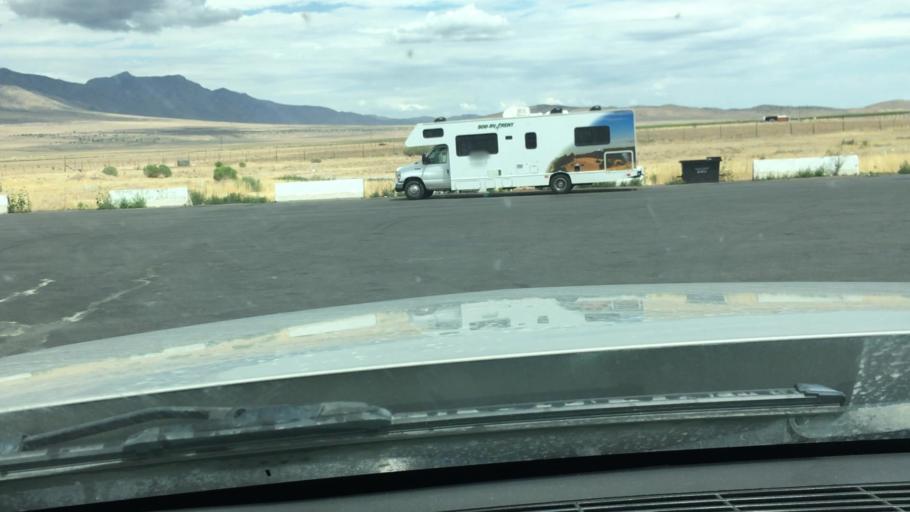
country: US
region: Utah
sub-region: Sanpete County
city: Gunnison
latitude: 39.2556
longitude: -112.1179
